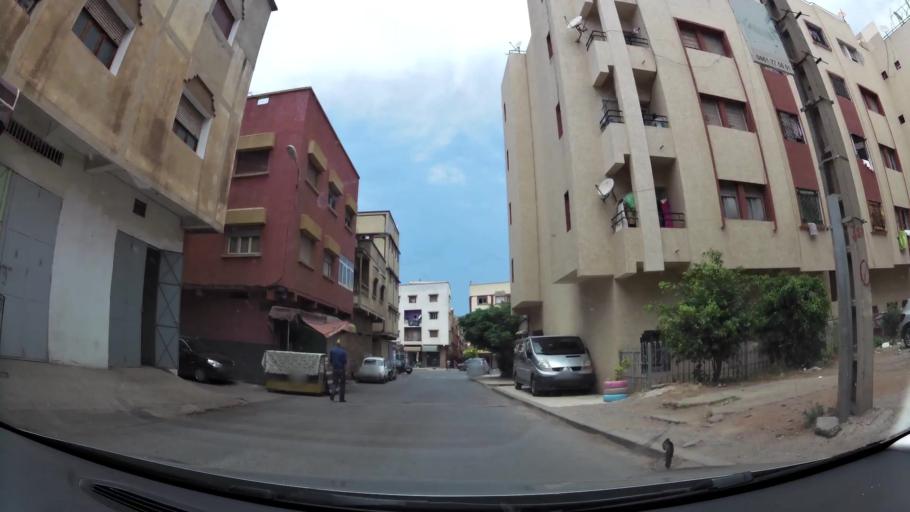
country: MA
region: Rabat-Sale-Zemmour-Zaer
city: Sale
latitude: 34.0578
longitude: -6.7865
